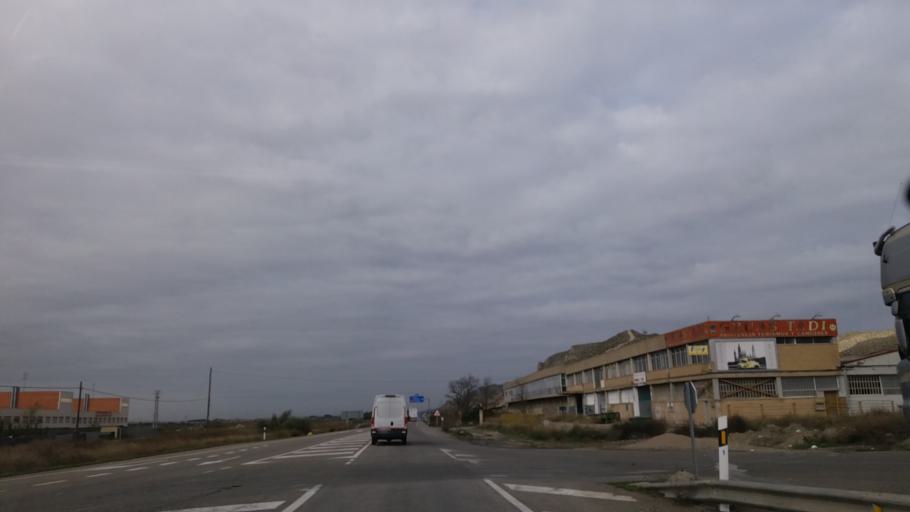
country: ES
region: Aragon
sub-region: Provincia de Zaragoza
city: Villafranca de Ebro
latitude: 41.5765
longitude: -0.6461
